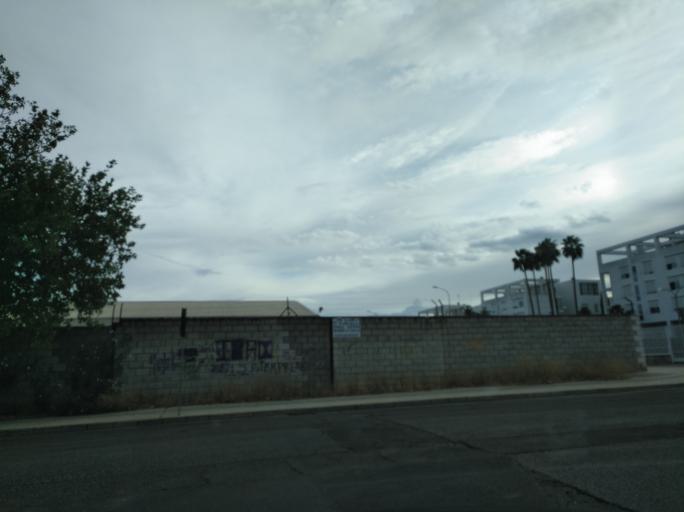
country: ES
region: Extremadura
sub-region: Provincia de Badajoz
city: Badajoz
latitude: 38.8837
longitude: -7.0141
